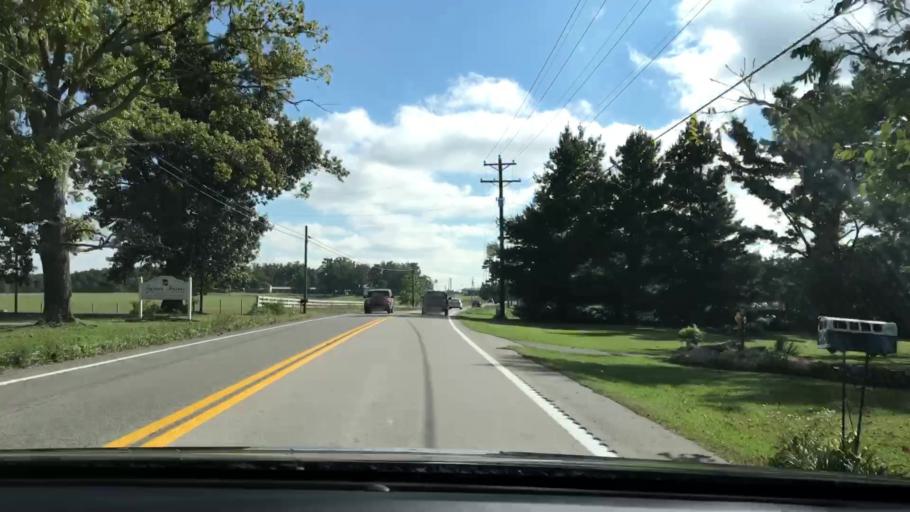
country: US
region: Tennessee
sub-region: Fentress County
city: Grimsley
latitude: 36.1988
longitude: -85.0200
